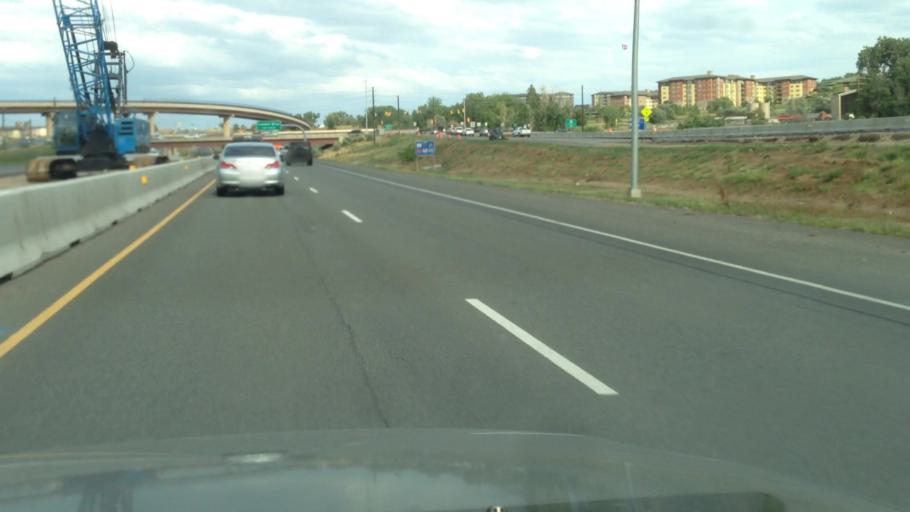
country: US
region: Colorado
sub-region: Arapahoe County
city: Columbine Valley
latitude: 39.5648
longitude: -105.0367
